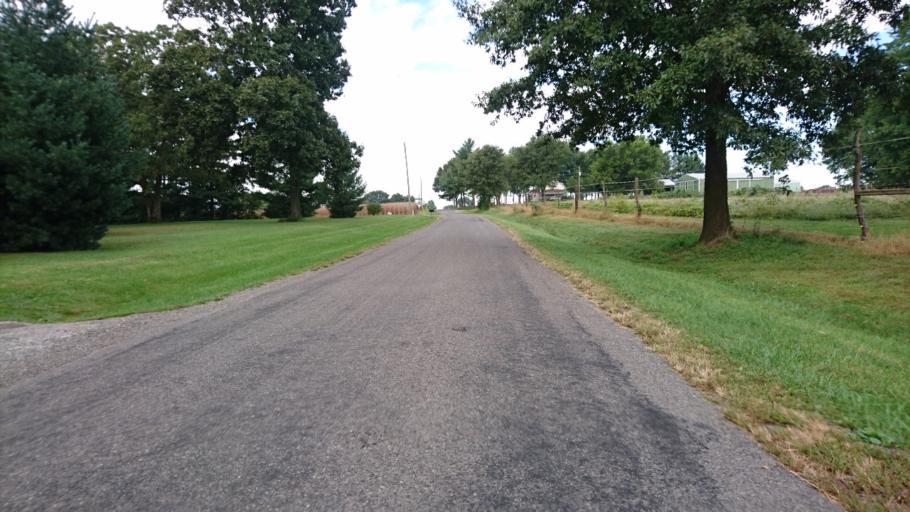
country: US
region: Illinois
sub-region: Macoupin County
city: Staunton
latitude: 38.9902
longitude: -89.7162
